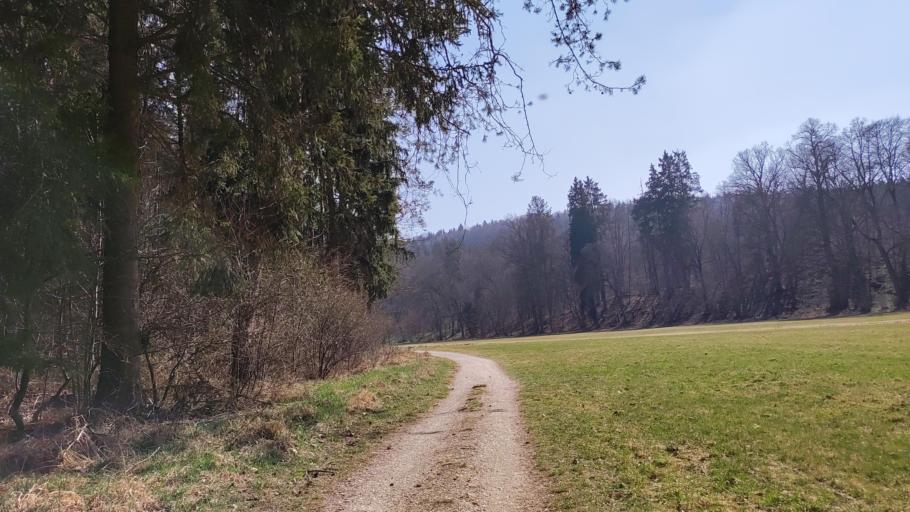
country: DE
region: Baden-Wuerttemberg
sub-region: Tuebingen Region
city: Borslingen
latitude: 48.5200
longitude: 10.0494
